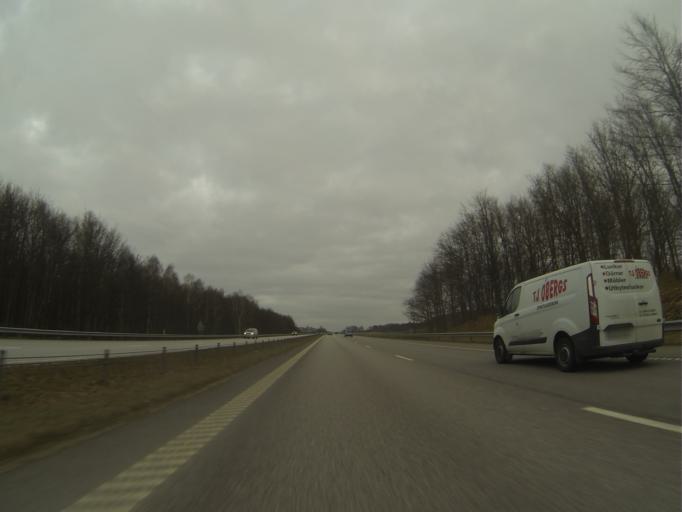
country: SE
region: Skane
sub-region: Malmo
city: Oxie
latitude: 55.5466
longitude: 13.1413
